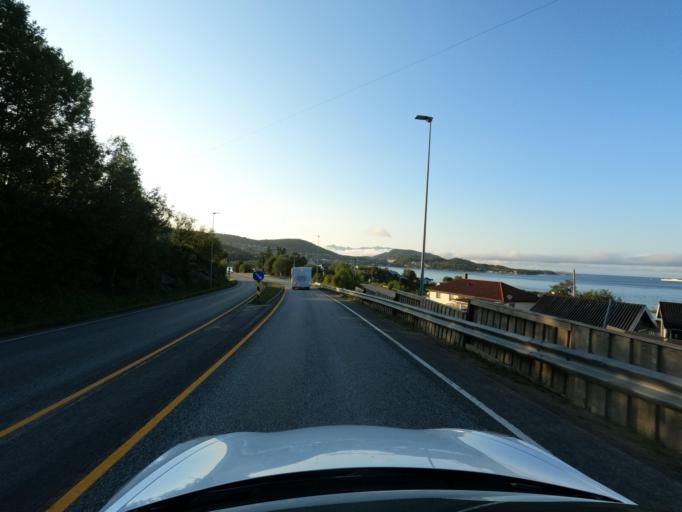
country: NO
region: Troms
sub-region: Harstad
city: Harstad
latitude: 68.7591
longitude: 16.5676
